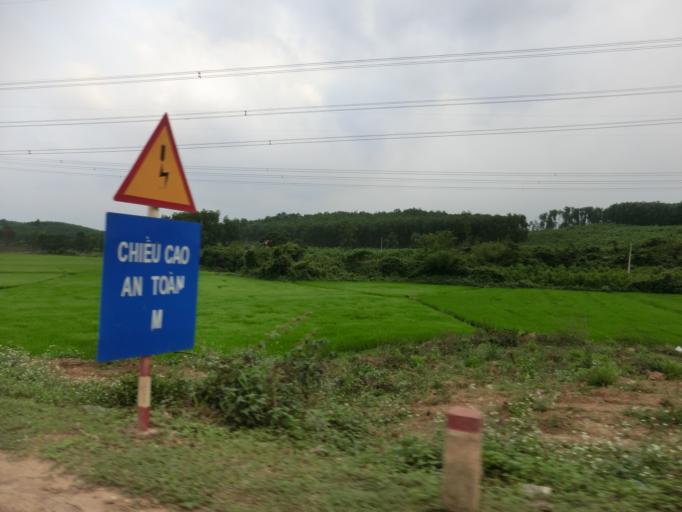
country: VN
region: Quang Binh
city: Kien Giang
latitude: 17.1210
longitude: 106.7931
